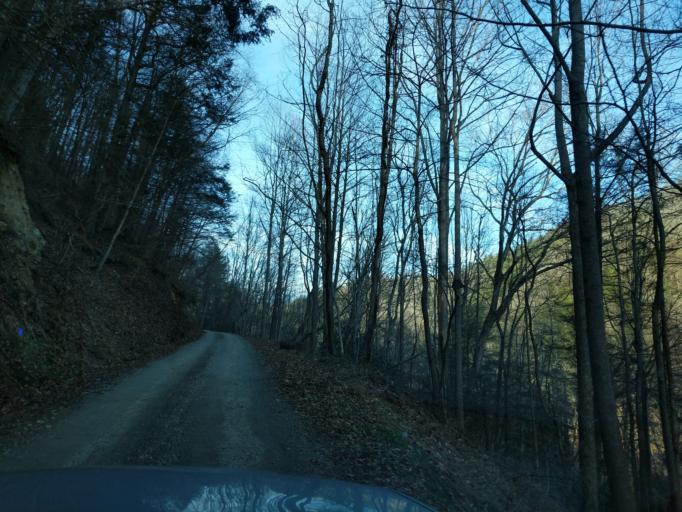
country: US
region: North Carolina
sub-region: Haywood County
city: Cove Creek
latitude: 35.7267
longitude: -83.0261
